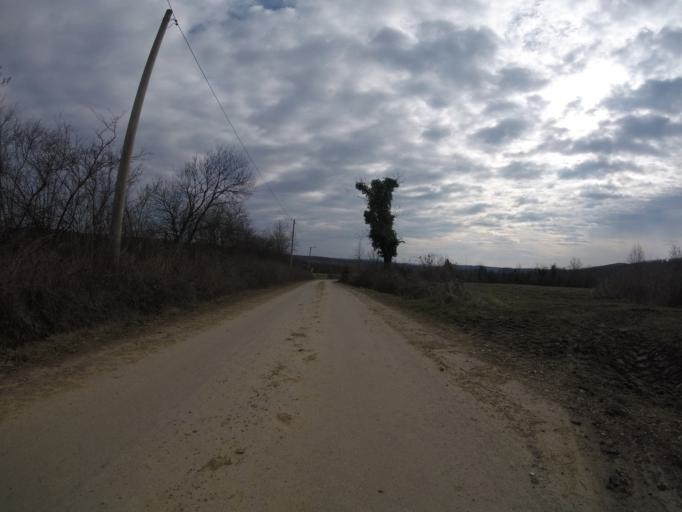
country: HR
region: Sisacko-Moslavacka
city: Glina
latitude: 45.4613
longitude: 16.0512
